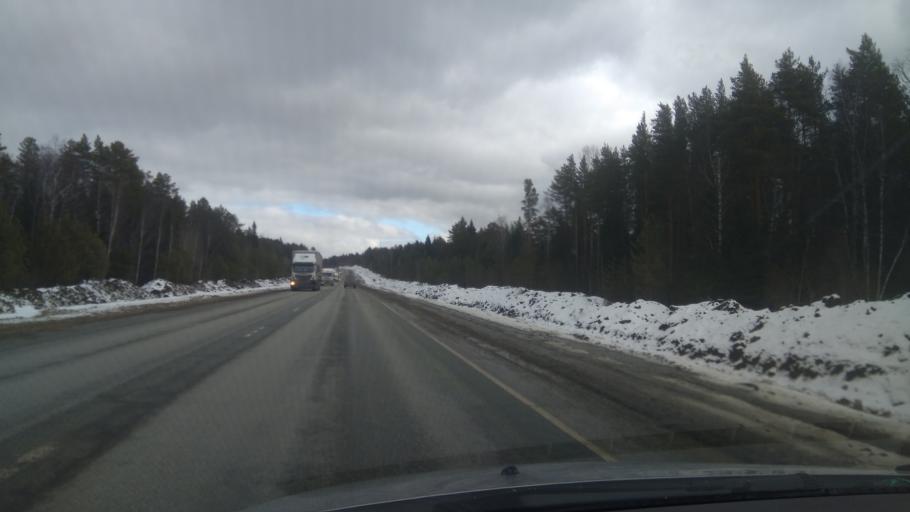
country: RU
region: Sverdlovsk
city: Bisert'
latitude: 56.8295
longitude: 58.9674
